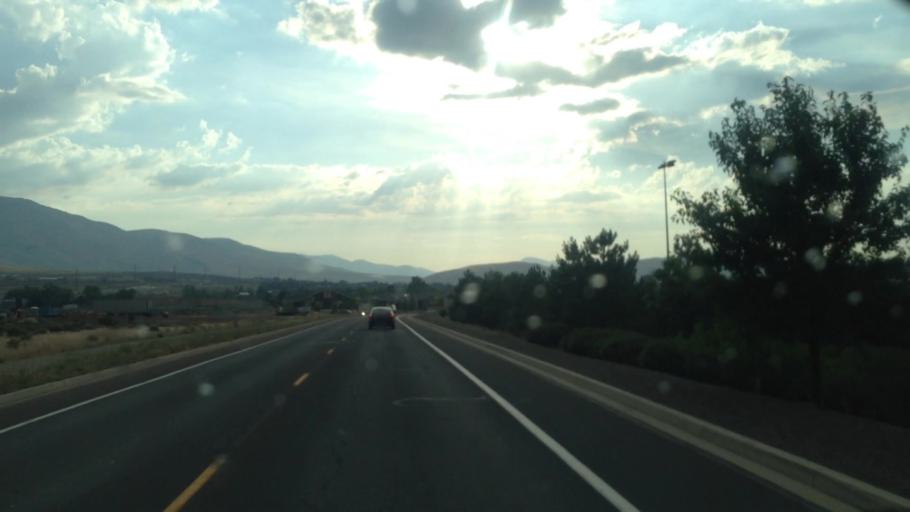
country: US
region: Nevada
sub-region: Washoe County
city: Lemmon Valley
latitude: 39.6216
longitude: -119.8652
